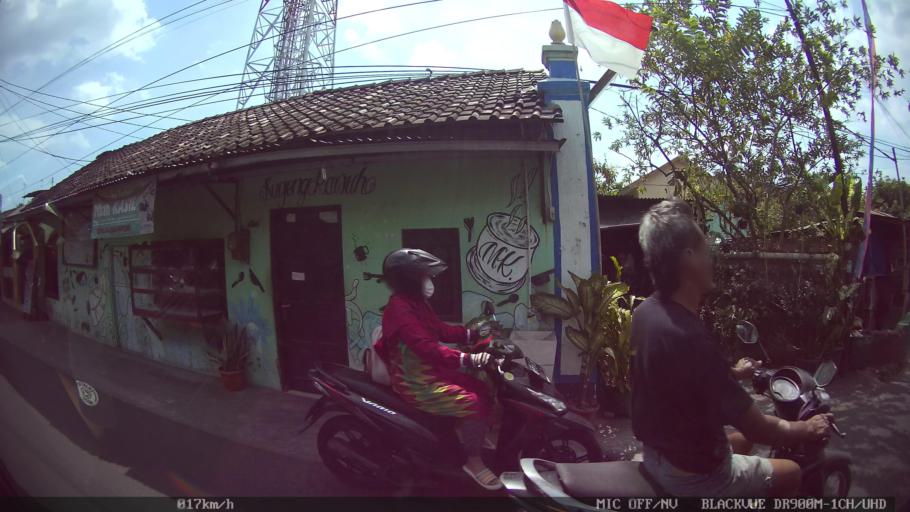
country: ID
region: Daerah Istimewa Yogyakarta
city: Kasihan
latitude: -7.8124
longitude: 110.3376
